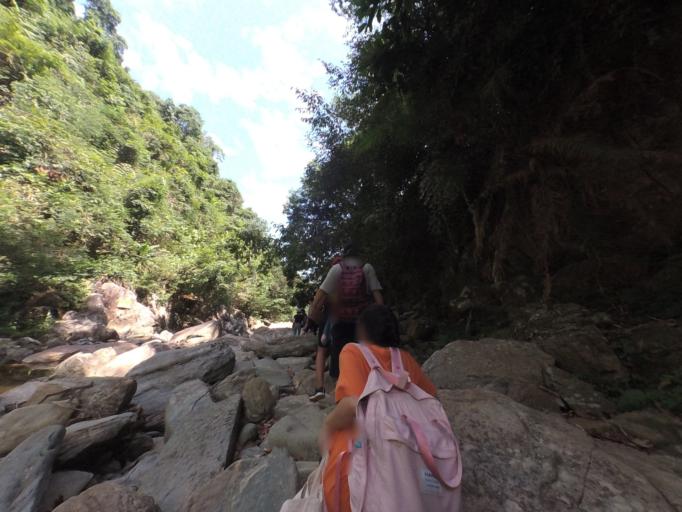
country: VN
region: Thua Thien-Hue
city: A Luoi
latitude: 16.3063
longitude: 107.3242
